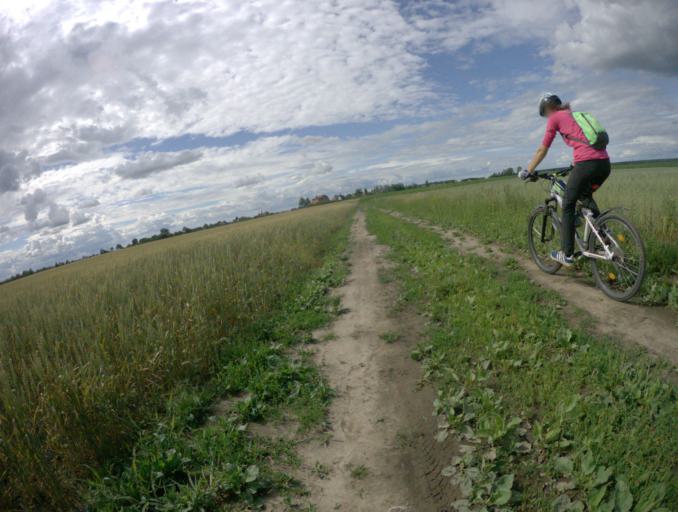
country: RU
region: Vladimir
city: Kideksha
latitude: 56.3243
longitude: 40.5996
